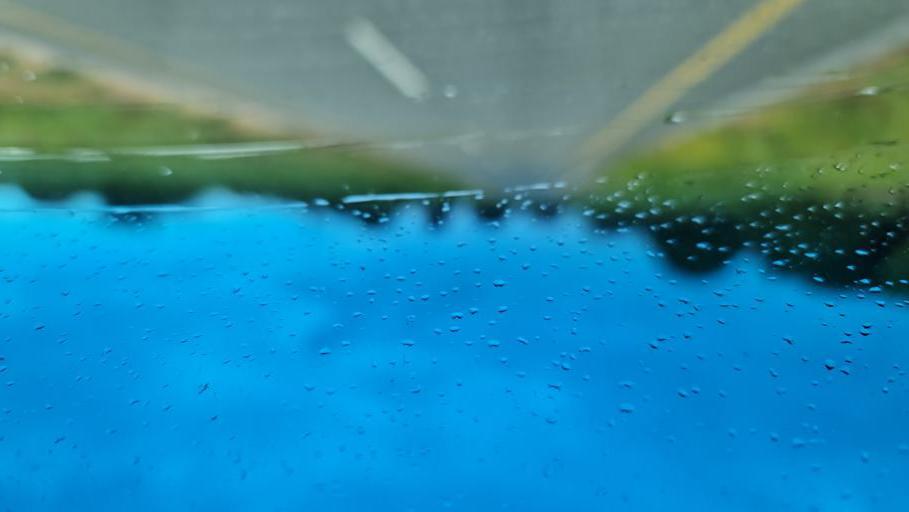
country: MZ
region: Nampula
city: Nampula
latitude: -15.4982
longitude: 39.3321
